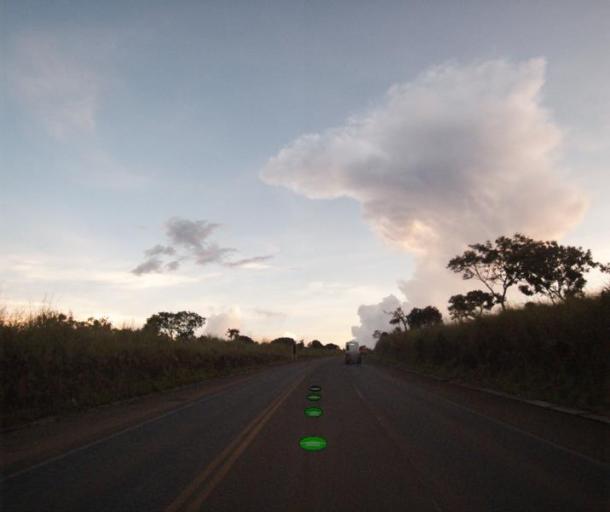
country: BR
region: Goias
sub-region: Uruacu
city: Uruacu
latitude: -14.5090
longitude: -49.1482
